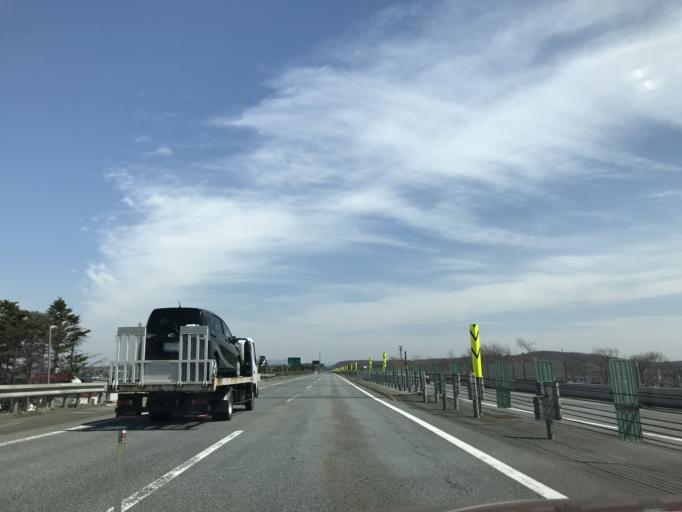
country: JP
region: Hokkaido
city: Iwamizawa
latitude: 43.1692
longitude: 141.7566
